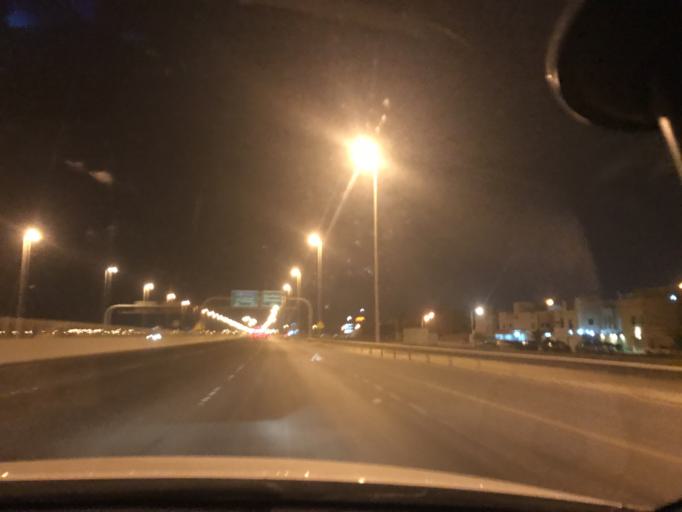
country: BH
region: Muharraq
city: Al Muharraq
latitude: 26.2865
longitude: 50.6396
